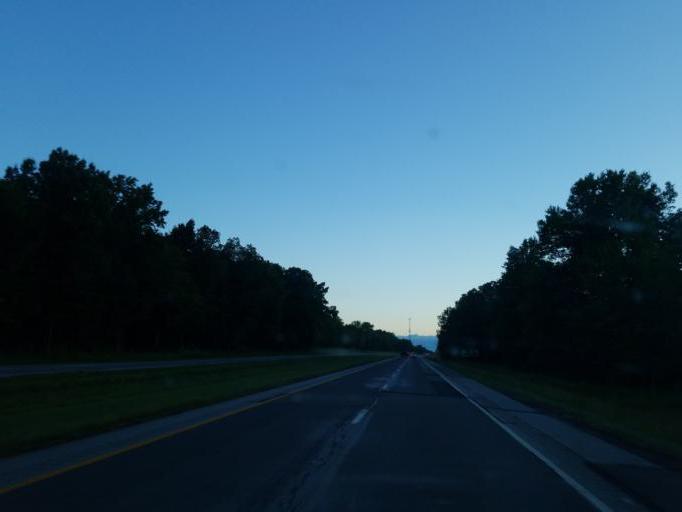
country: US
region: Ohio
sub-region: Wayne County
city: Doylestown
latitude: 40.9800
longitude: -81.6626
